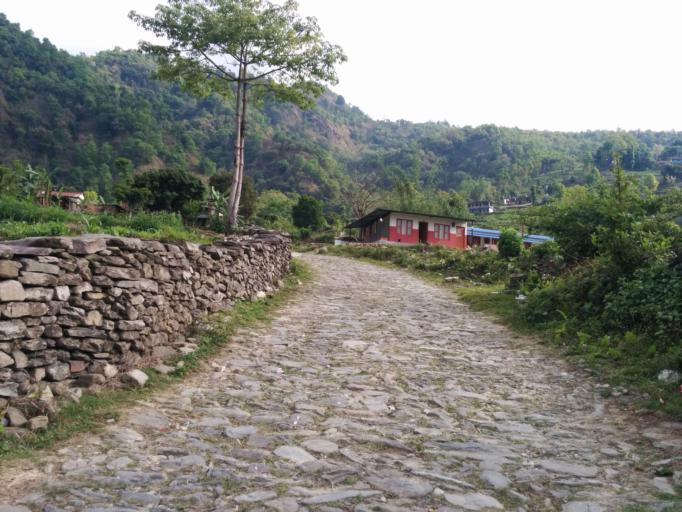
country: NP
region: Western Region
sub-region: Gandaki Zone
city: Pokhara
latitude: 28.2285
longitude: 83.9494
